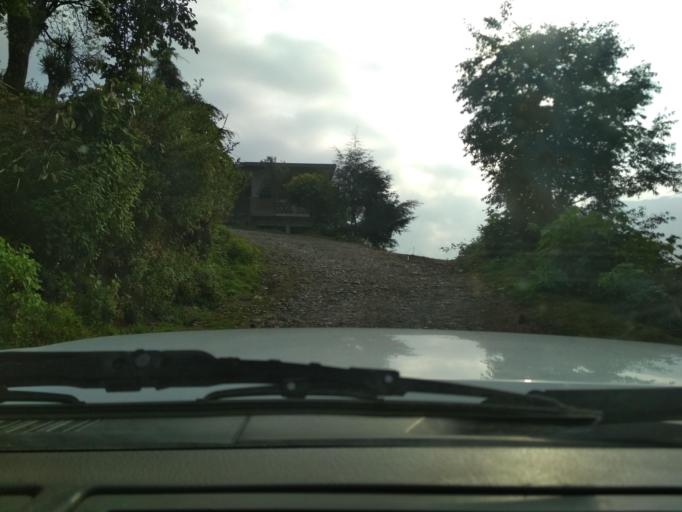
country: MX
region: Veracruz
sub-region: Camerino Z. Mendoza
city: Necoxtla
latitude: 18.7555
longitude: -97.1548
